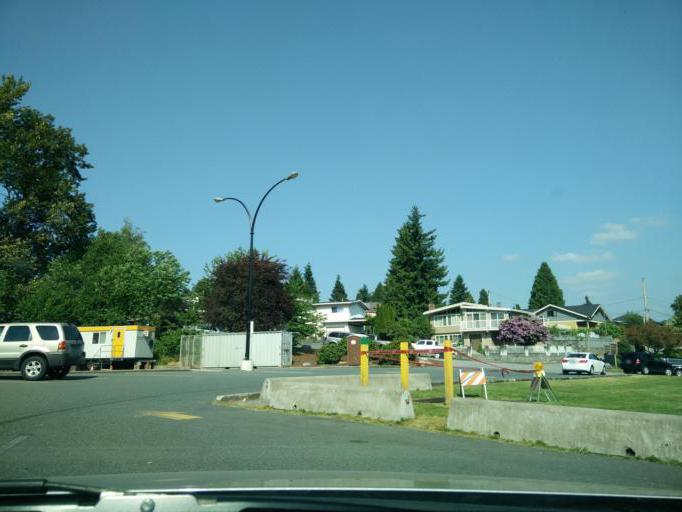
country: CA
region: British Columbia
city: Burnaby
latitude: 49.2649
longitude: -122.9775
